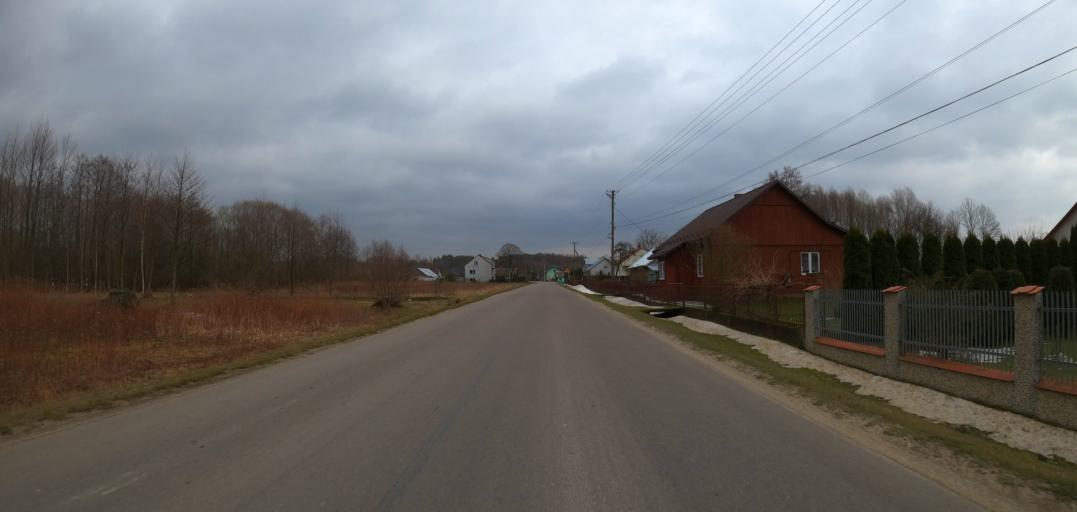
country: PL
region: Subcarpathian Voivodeship
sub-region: Powiat debicki
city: Pilzno
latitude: 49.9797
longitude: 21.3372
